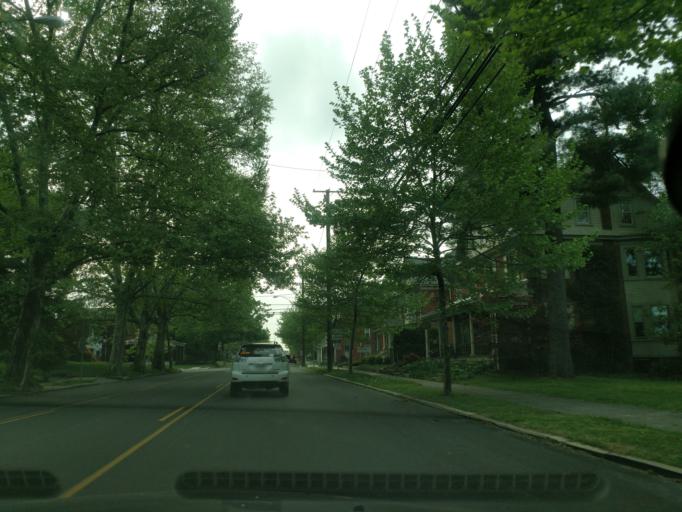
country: US
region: Pennsylvania
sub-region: Berks County
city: Wernersville
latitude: 40.3313
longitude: -76.0871
